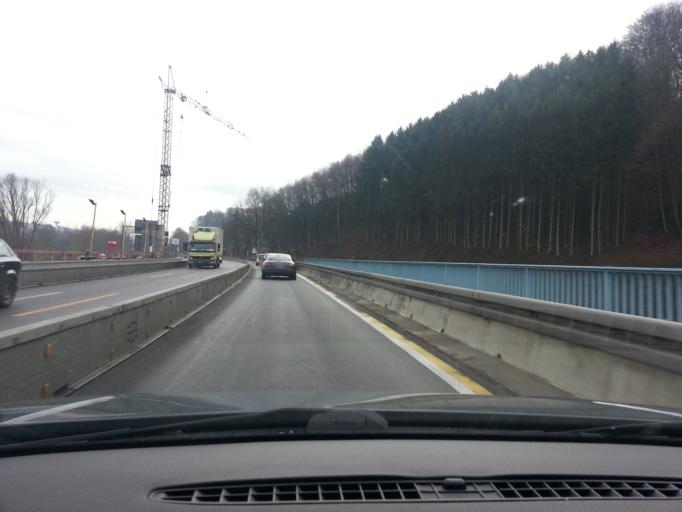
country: DE
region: Rheinland-Pfalz
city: Zweibrucken
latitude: 49.2643
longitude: 7.3138
